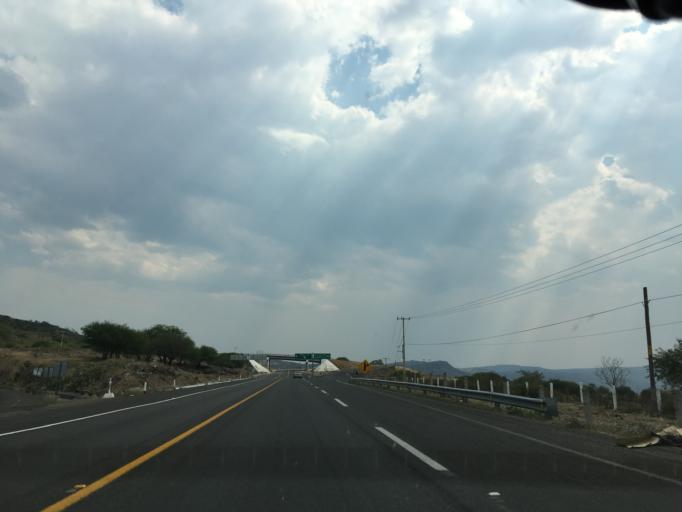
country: MX
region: Michoacan
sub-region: Cuitzeo
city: San Juan Benito Juarez (San Juan Tararameo)
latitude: 19.9153
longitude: -101.1457
